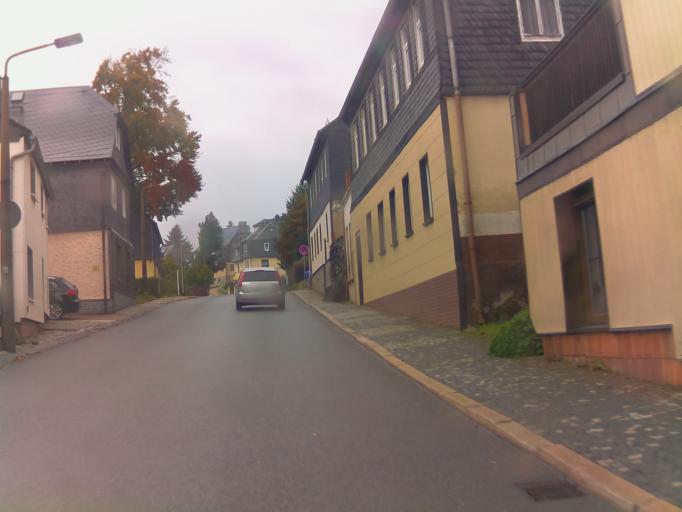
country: DE
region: Thuringia
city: Wurzbach
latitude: 50.4624
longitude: 11.5355
